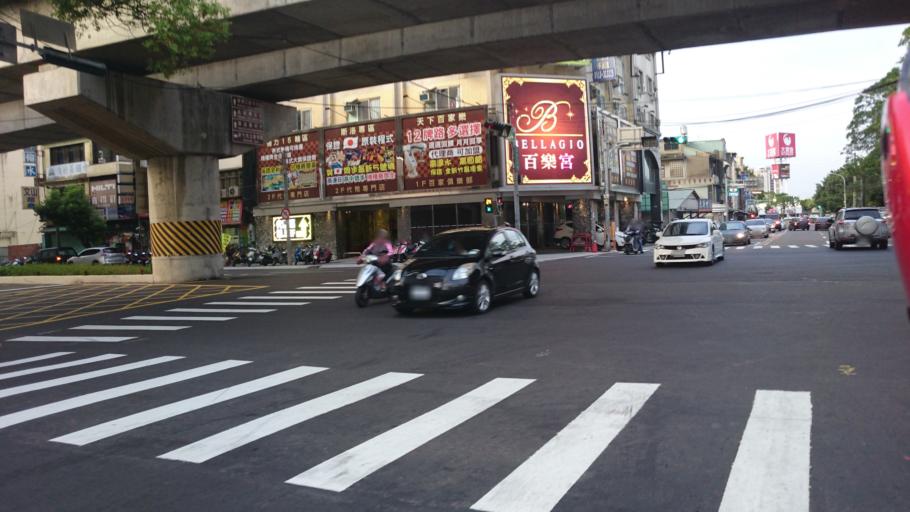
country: TW
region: Taiwan
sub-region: Hsinchu
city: Hsinchu
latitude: 24.8021
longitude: 120.9831
